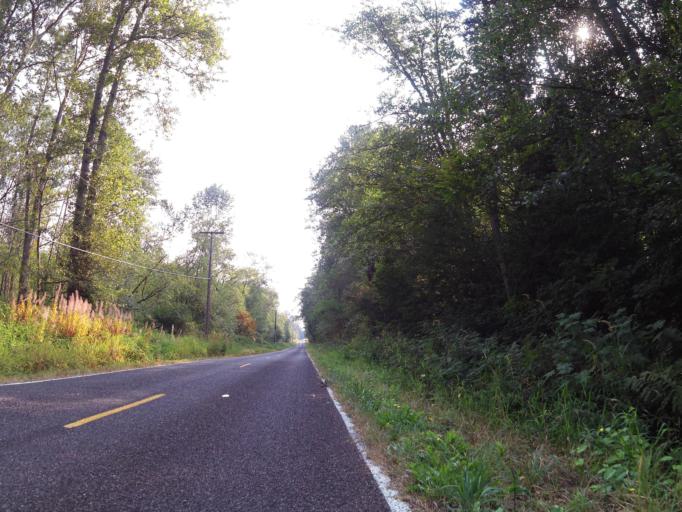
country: US
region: Washington
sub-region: Whatcom County
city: Birch Bay
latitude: 48.8630
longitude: -122.7148
